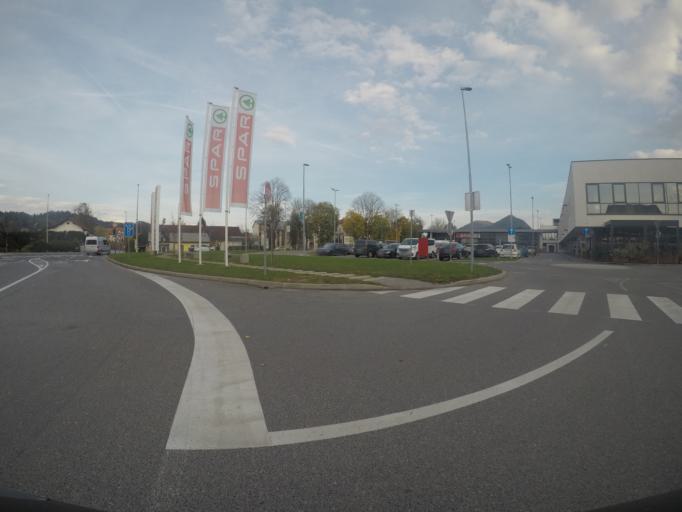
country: SI
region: Medvode
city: Medvode
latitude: 46.1395
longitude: 14.4139
